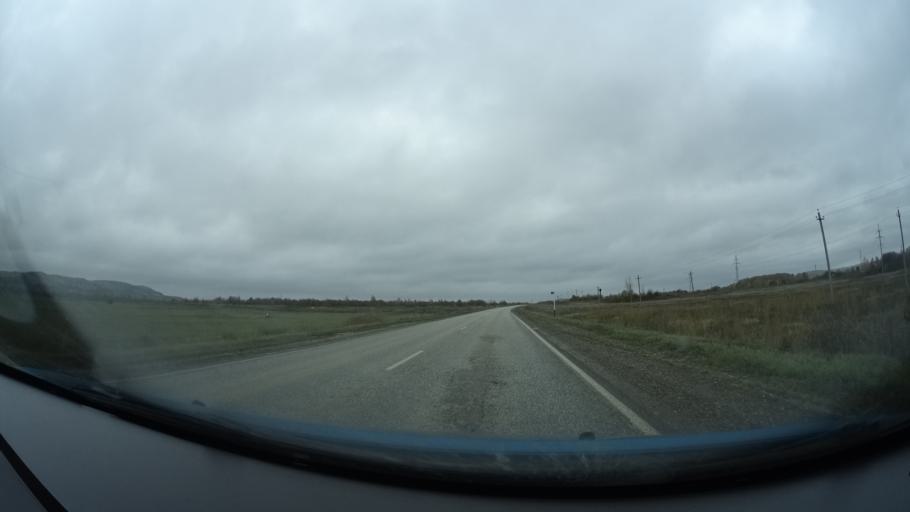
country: RU
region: Perm
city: Barda
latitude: 57.0871
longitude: 55.5397
